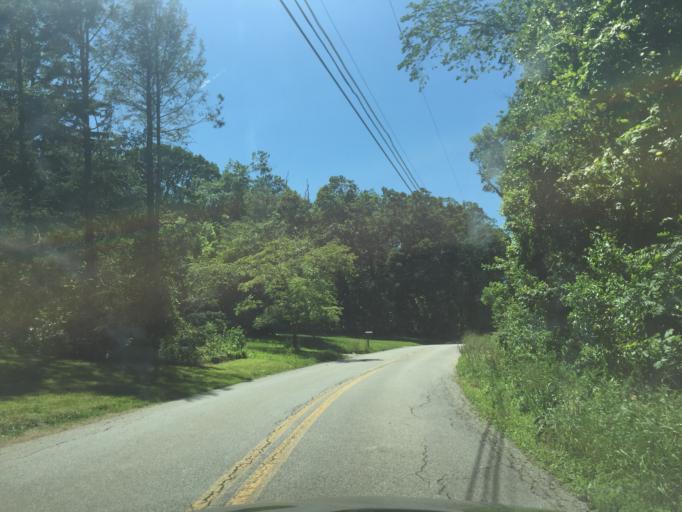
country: US
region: Maryland
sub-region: Carroll County
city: Manchester
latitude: 39.6227
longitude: -76.9097
